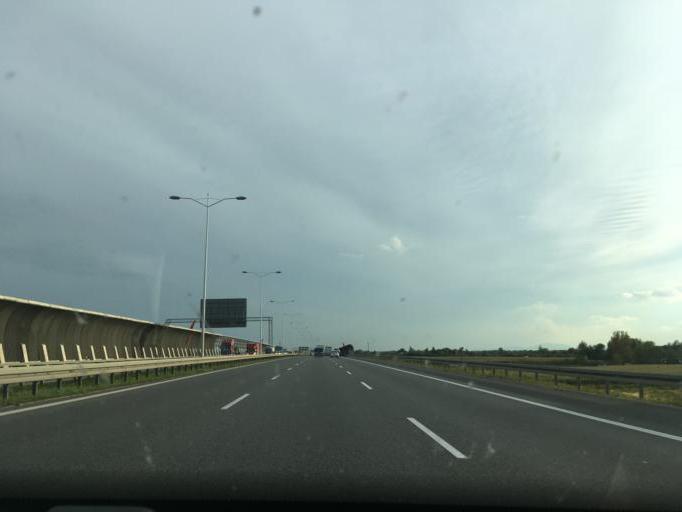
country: PL
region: Lower Silesian Voivodeship
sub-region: Powiat wroclawski
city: Smolec
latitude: 51.0981
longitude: 16.9327
